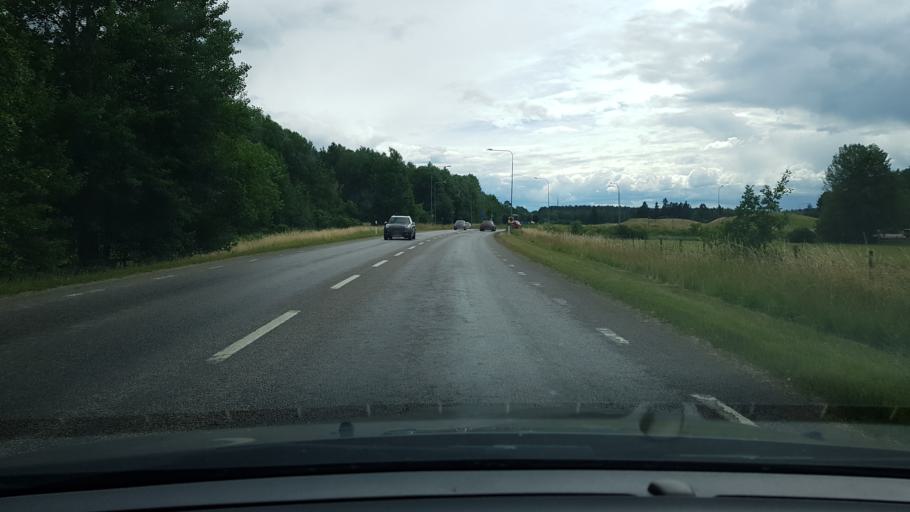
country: SE
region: Uppsala
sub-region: Uppsala Kommun
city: Saevja
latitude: 59.8186
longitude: 17.6982
